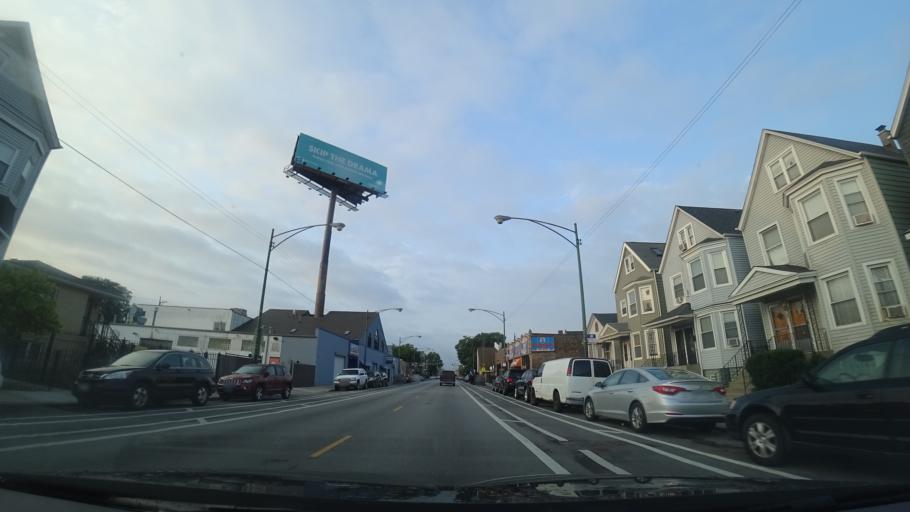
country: US
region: Illinois
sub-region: Cook County
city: Lincolnwood
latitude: 41.9371
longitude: -87.7076
